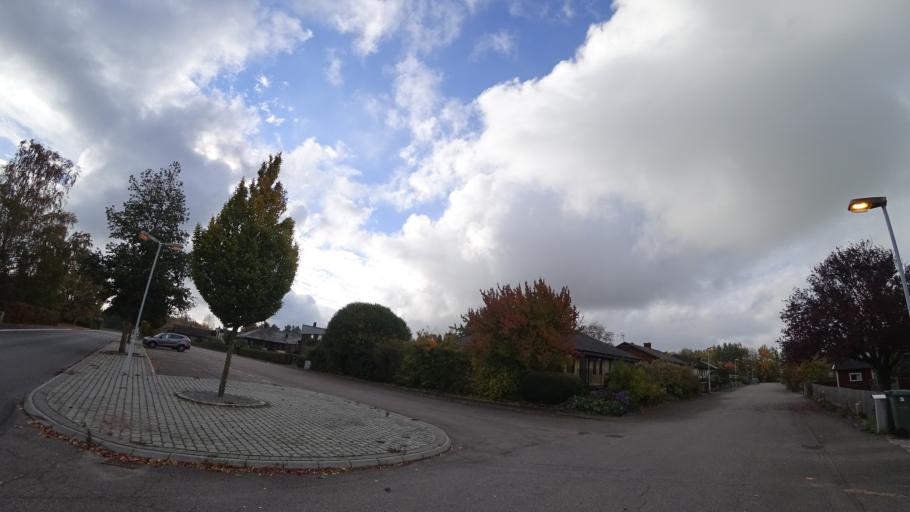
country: SE
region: Skane
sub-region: Staffanstorps Kommun
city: Staffanstorp
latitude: 55.6470
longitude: 13.1919
